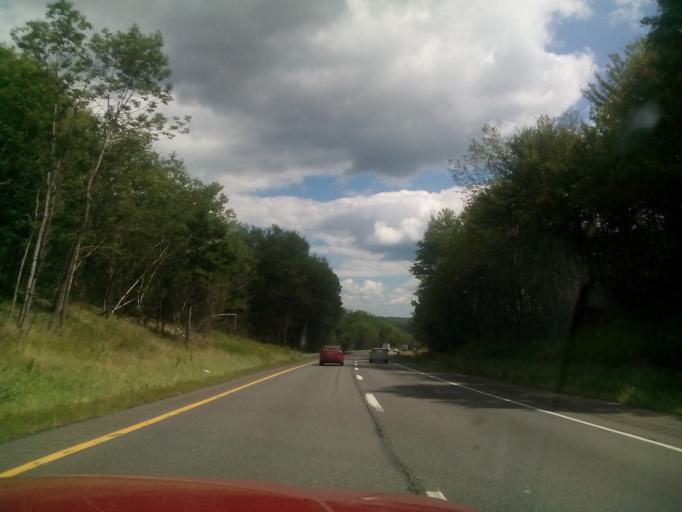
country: US
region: Pennsylvania
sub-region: Monroe County
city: Tannersville
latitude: 41.0608
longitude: -75.3311
